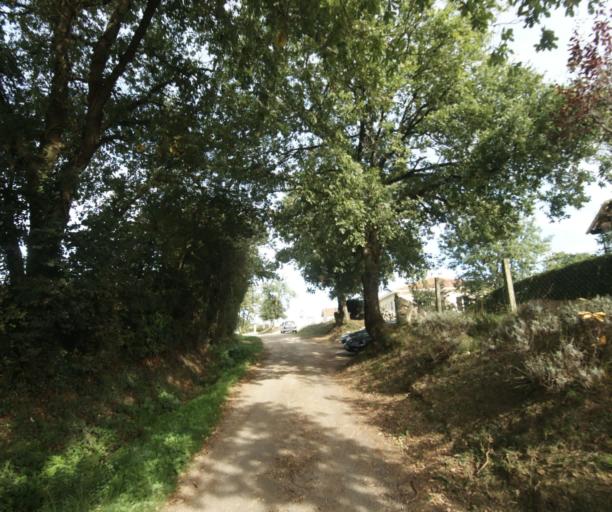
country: FR
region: Midi-Pyrenees
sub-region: Departement du Gers
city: Eauze
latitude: 43.8836
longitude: 0.1325
